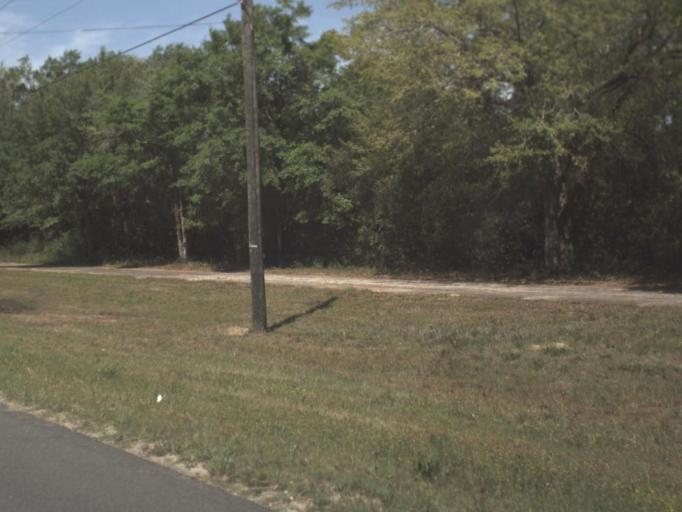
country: US
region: Florida
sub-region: Santa Rosa County
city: East Milton
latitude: 30.6262
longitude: -87.0115
